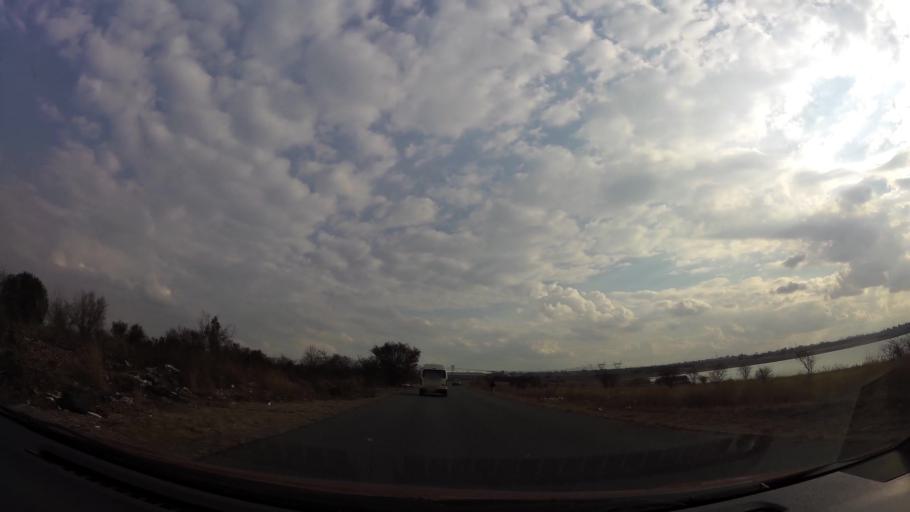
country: ZA
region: Gauteng
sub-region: Sedibeng District Municipality
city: Vereeniging
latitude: -26.6925
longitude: 27.8965
